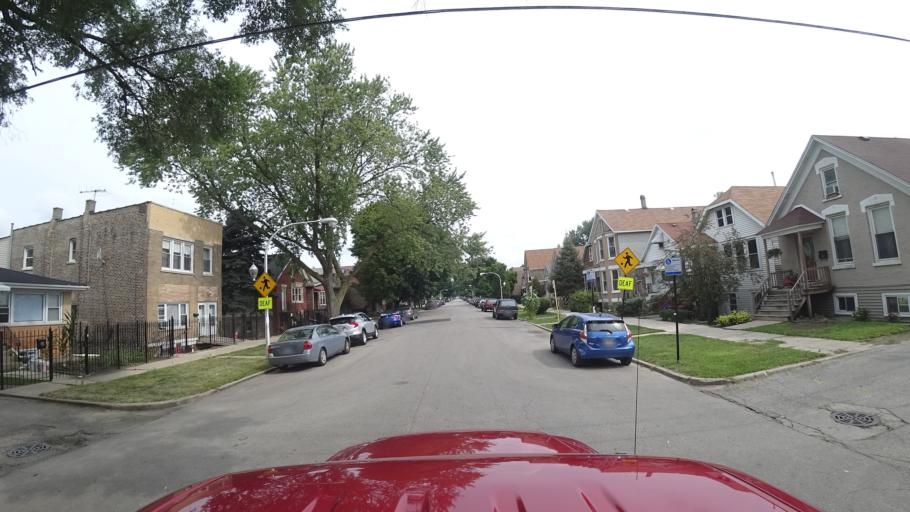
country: US
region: Illinois
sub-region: Cook County
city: Chicago
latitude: 41.8235
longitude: -87.6714
